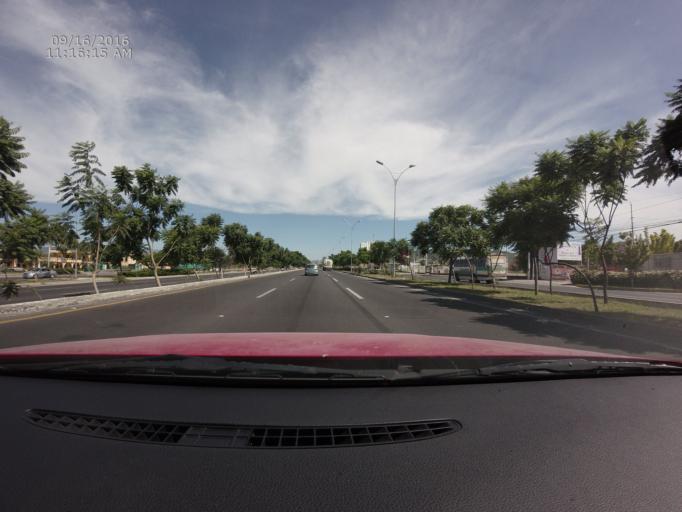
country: MX
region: Queretaro
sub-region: Queretaro
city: El Salitre
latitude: 20.6583
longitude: -100.4323
